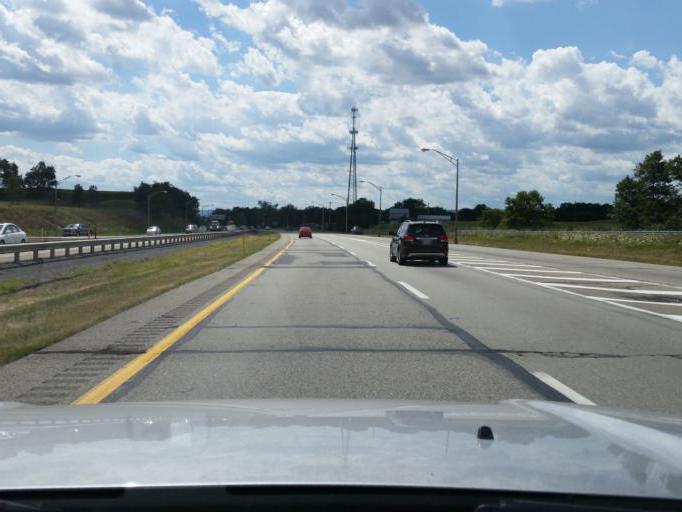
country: US
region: Pennsylvania
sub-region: Bedford County
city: Earlston
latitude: 39.9870
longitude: -78.2596
